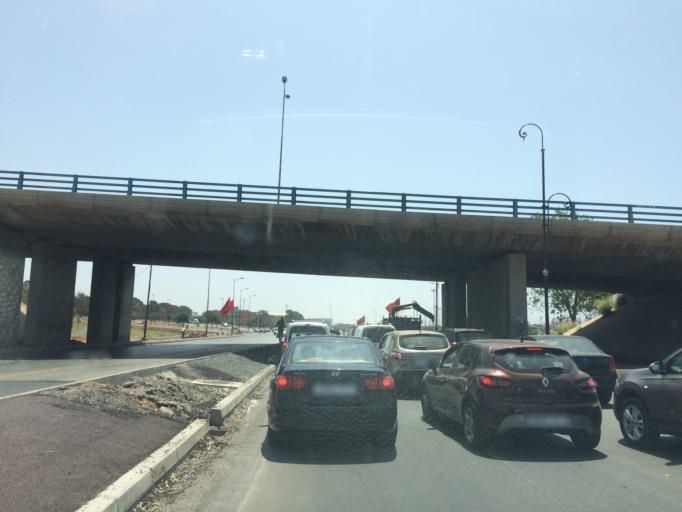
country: MA
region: Rabat-Sale-Zemmour-Zaer
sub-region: Skhirate-Temara
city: Temara
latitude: 33.9730
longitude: -6.8800
